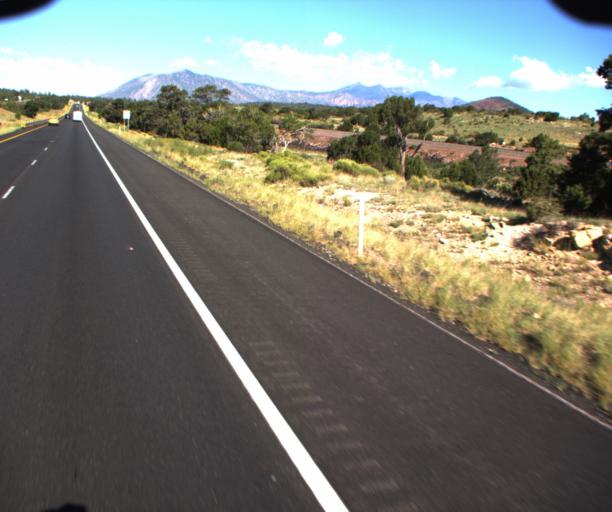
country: US
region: Arizona
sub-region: Coconino County
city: Flagstaff
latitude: 35.2037
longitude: -111.4861
